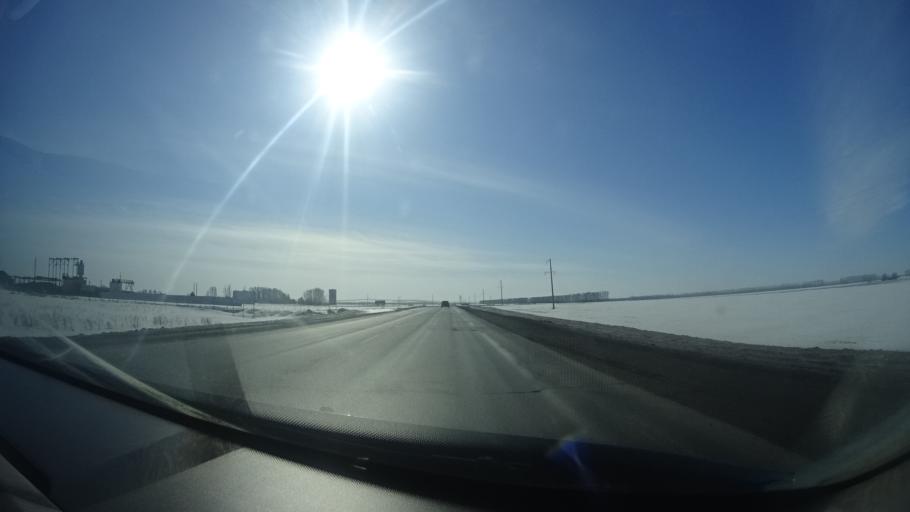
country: RU
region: Bashkortostan
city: Mikhaylovka
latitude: 54.9567
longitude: 55.7572
